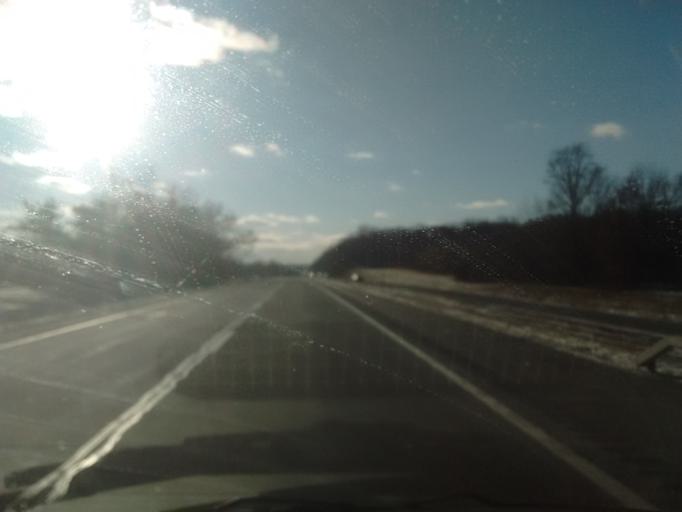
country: US
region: New York
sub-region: Orange County
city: Orange Lake
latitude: 41.5208
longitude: -74.1095
